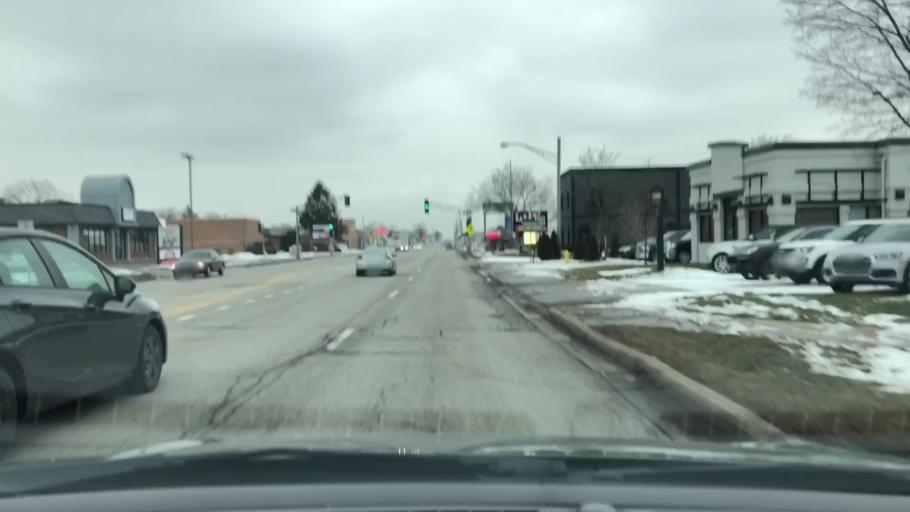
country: US
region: Illinois
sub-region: DuPage County
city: Westmont
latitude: 41.8100
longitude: -87.9803
